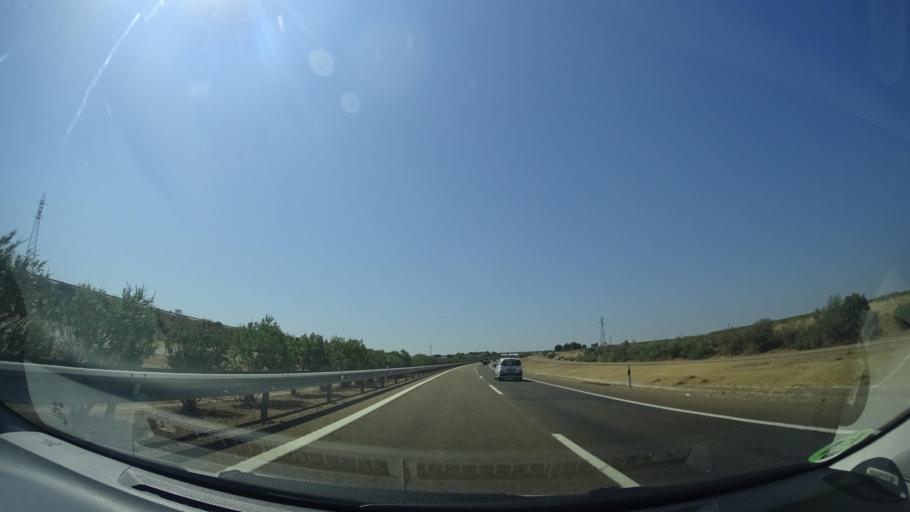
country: ES
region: Extremadura
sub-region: Provincia de Badajoz
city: Almendralejo
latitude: 38.6840
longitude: -6.3776
